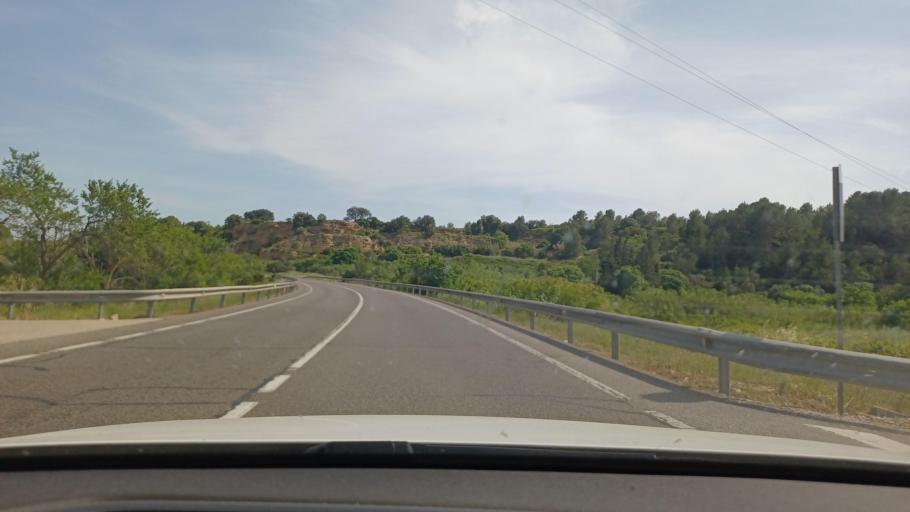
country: ES
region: Catalonia
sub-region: Provincia de Tarragona
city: Tortosa
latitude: 40.7894
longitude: 0.4962
